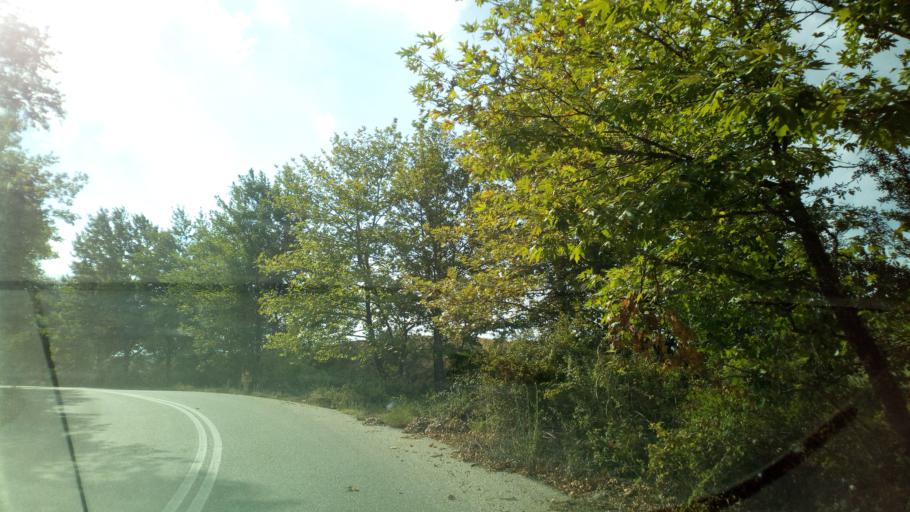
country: GR
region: Central Macedonia
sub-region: Nomos Chalkidikis
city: Galatista
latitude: 40.5271
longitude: 23.3434
